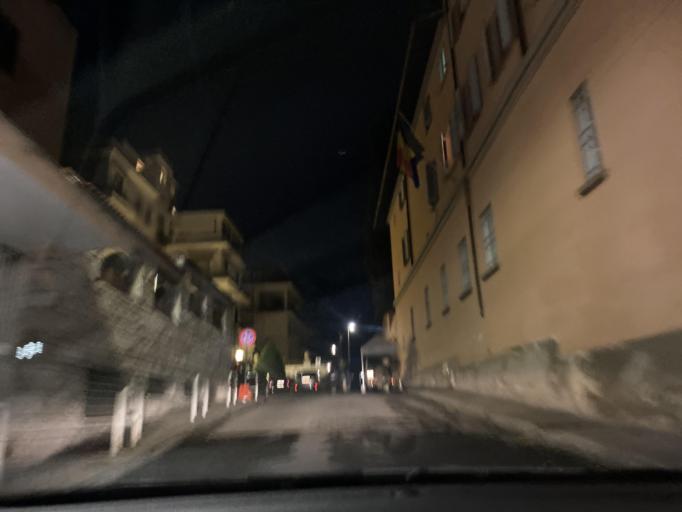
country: VA
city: Vatican City
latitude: 41.9200
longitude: 12.4808
